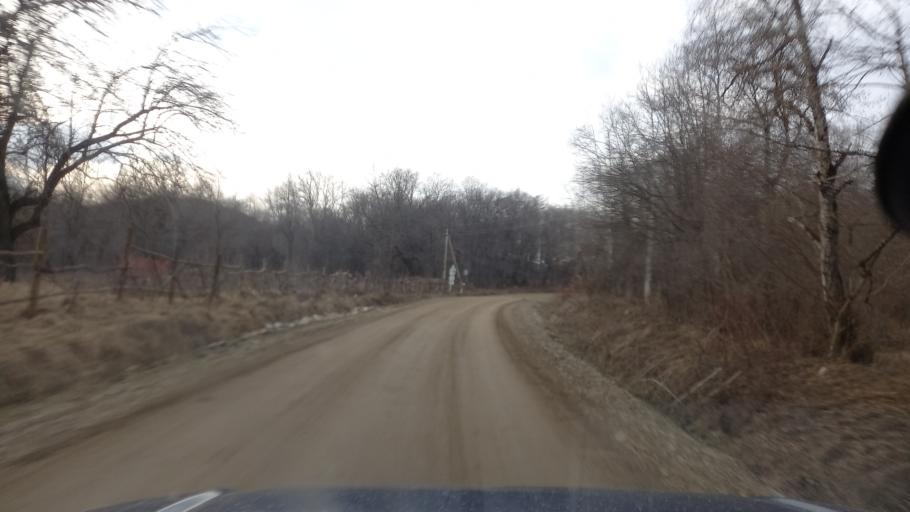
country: RU
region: Adygeya
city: Kamennomostskiy
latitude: 44.1383
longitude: 40.2632
